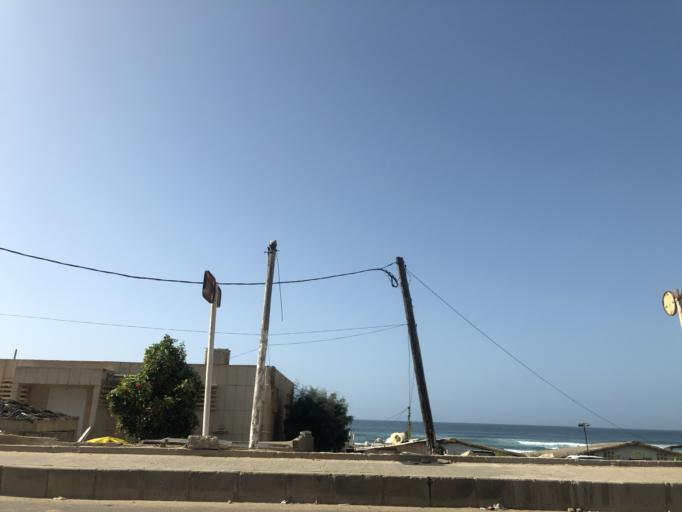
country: SN
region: Dakar
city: Mermoz Boabab
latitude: 14.7541
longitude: -17.4960
